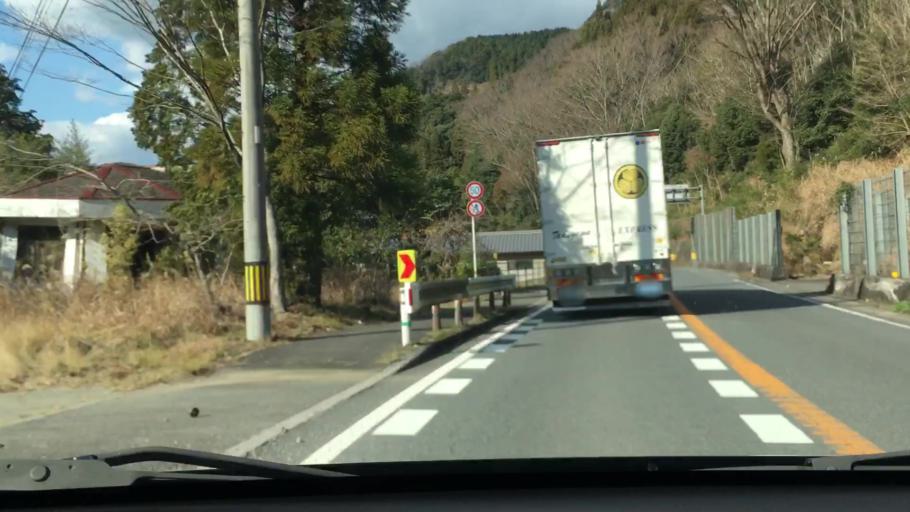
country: JP
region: Oita
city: Usuki
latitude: 32.9988
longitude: 131.7517
